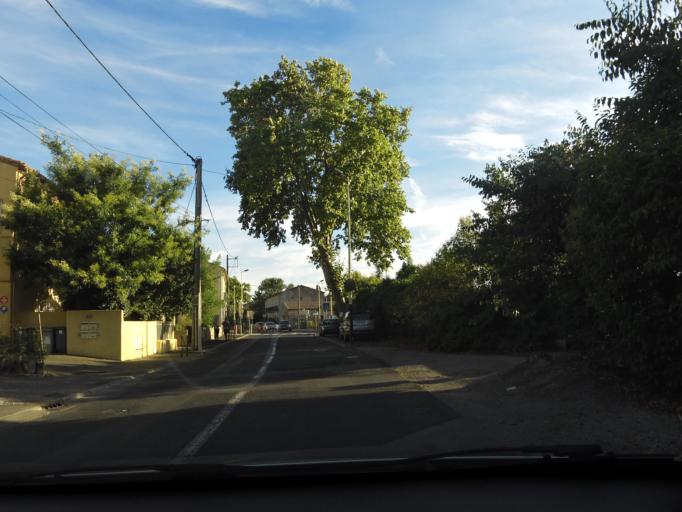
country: FR
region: Languedoc-Roussillon
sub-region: Departement de l'Herault
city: Prades-le-Lez
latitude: 43.7014
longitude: 3.8628
